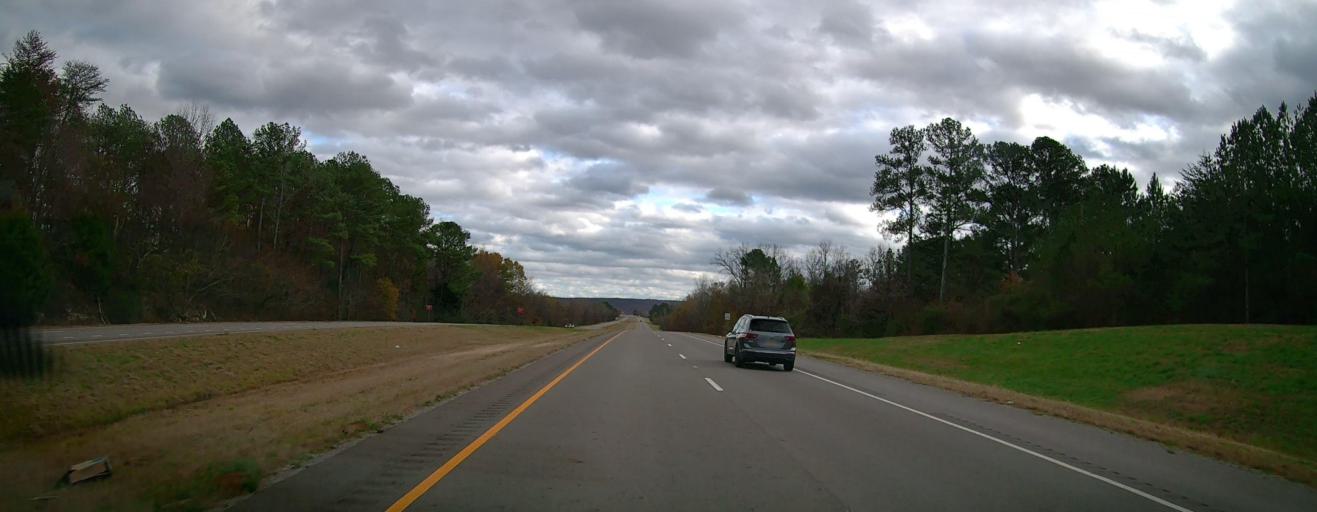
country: US
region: Alabama
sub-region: Morgan County
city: Danville
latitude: 34.3527
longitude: -87.0475
